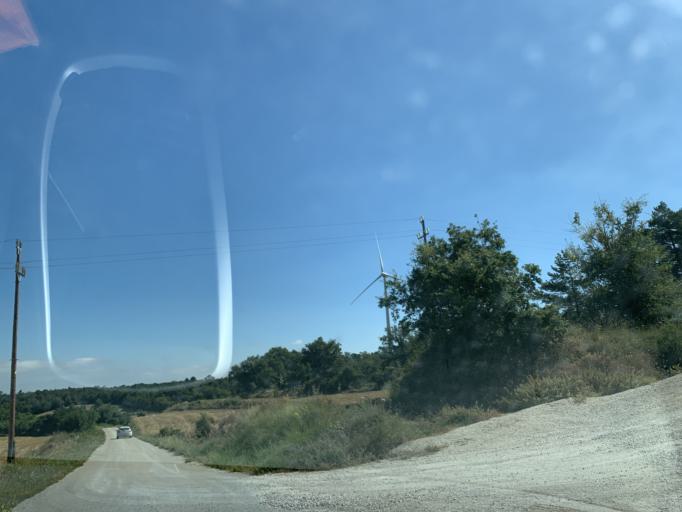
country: ES
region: Catalonia
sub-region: Provincia de Tarragona
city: Conesa
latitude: 41.5378
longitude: 1.2838
